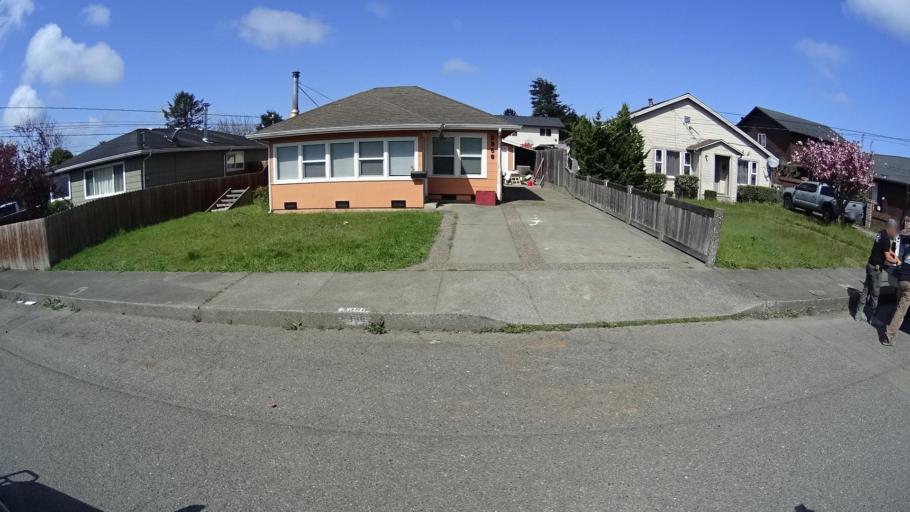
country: US
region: California
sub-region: Humboldt County
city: Cutten
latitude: 40.7778
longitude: -124.1614
